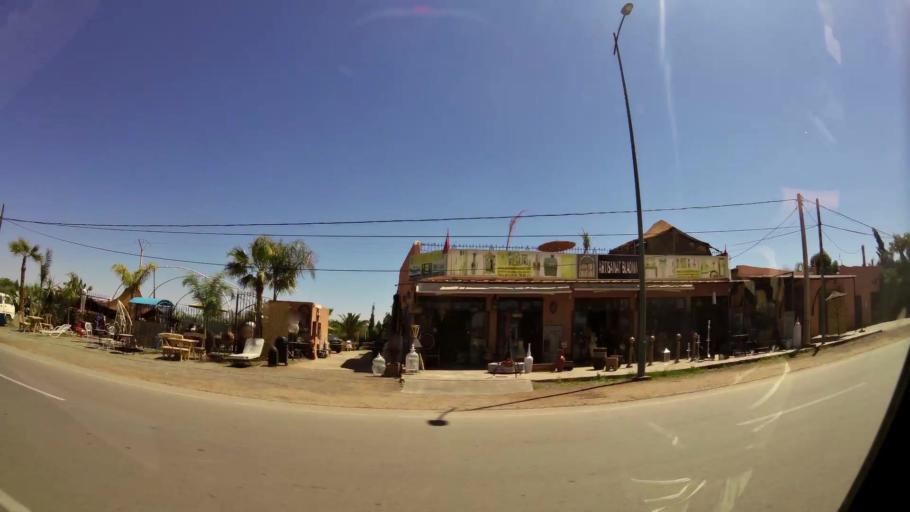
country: MA
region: Marrakech-Tensift-Al Haouz
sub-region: Marrakech
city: Marrakesh
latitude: 31.5582
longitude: -7.9770
